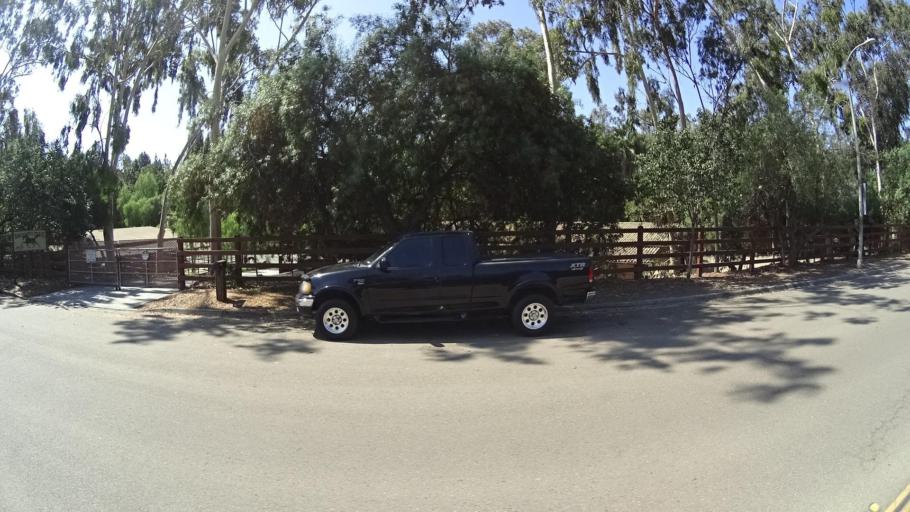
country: US
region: California
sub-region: San Diego County
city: Lake San Marcos
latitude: 33.1569
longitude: -117.2160
